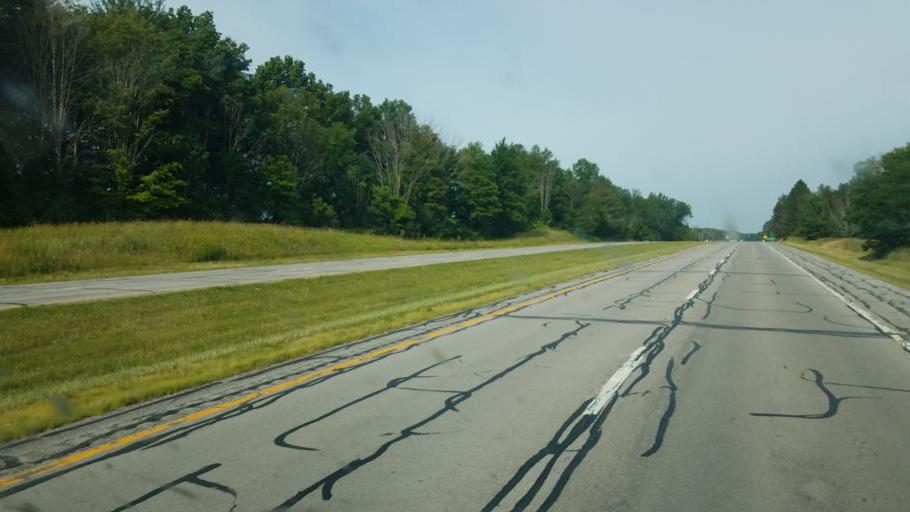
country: US
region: Ohio
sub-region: Medina County
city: Westfield Center
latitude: 41.0387
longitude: -81.9586
